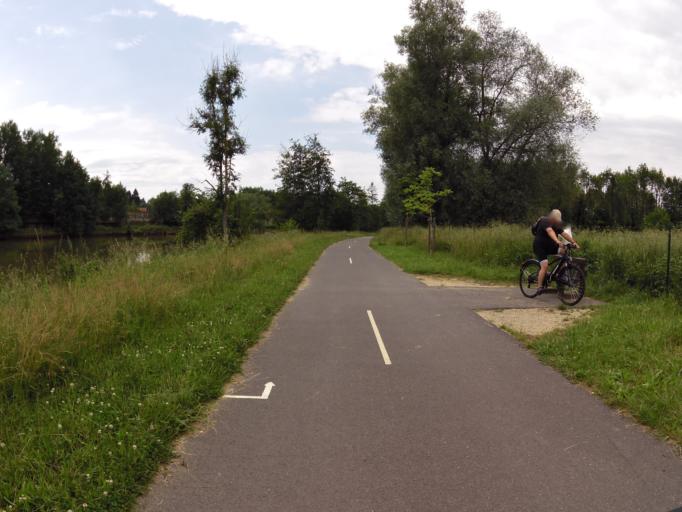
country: FR
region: Champagne-Ardenne
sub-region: Departement des Ardennes
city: Villers-Semeuse
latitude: 49.7558
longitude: 4.7360
